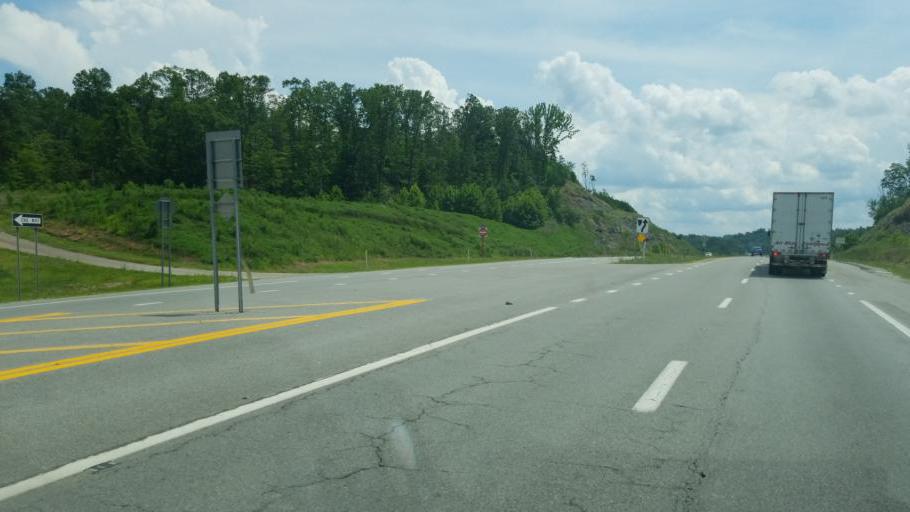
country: US
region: West Virginia
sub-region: Putnam County
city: Buffalo
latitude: 38.5764
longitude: -82.0162
